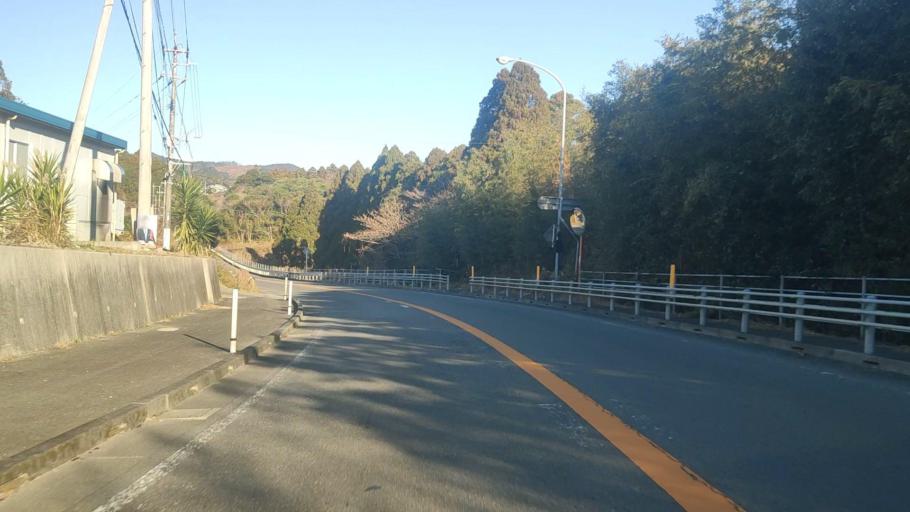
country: JP
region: Miyazaki
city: Nobeoka
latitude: 32.3451
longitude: 131.6244
